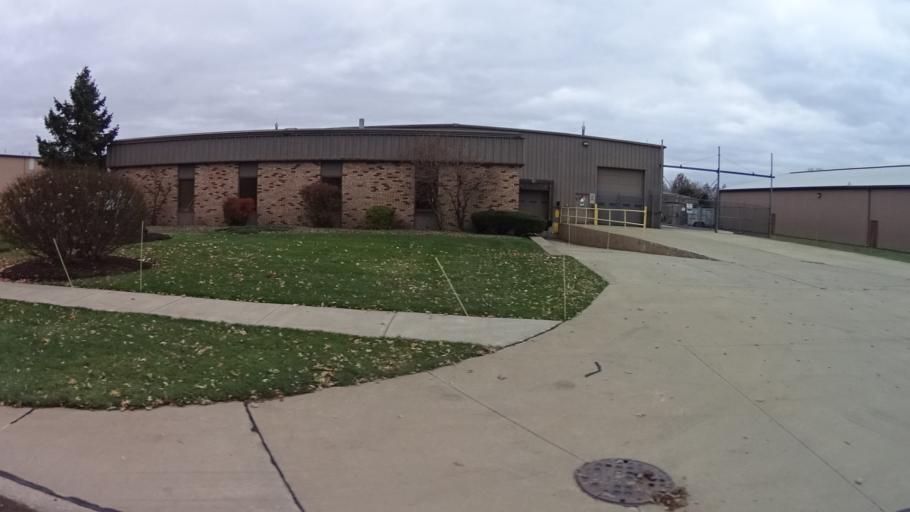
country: US
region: Ohio
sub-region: Lorain County
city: Avon Lake
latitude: 41.4816
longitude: -82.0396
